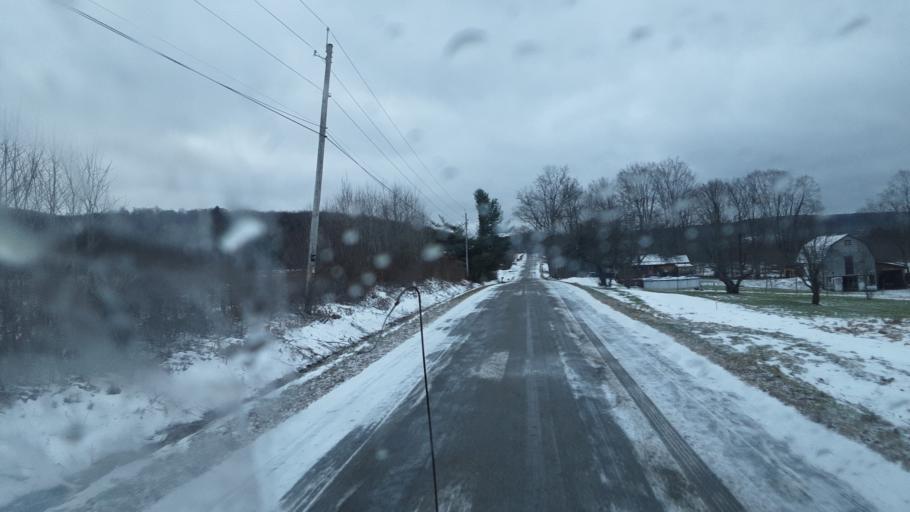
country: US
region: New York
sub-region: Allegany County
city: Friendship
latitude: 42.2938
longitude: -78.1581
